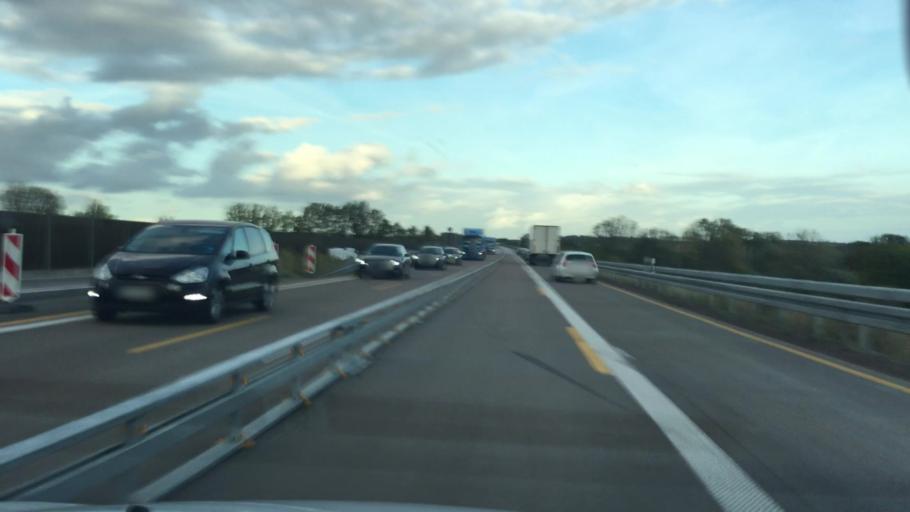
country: DE
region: Saxony-Anhalt
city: Wallwitz
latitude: 51.5692
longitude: 11.9397
